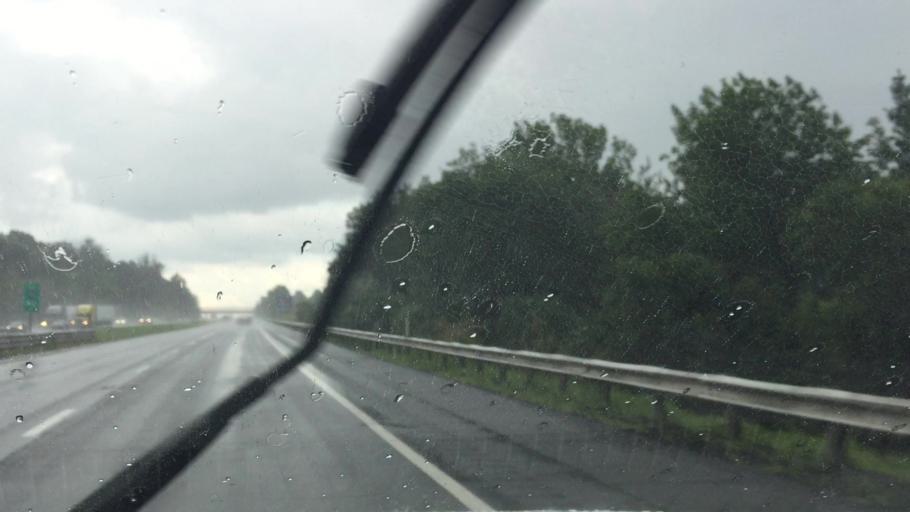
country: US
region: Massachusetts
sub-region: Berkshire County
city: Stockbridge
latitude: 42.3026
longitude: -73.3229
